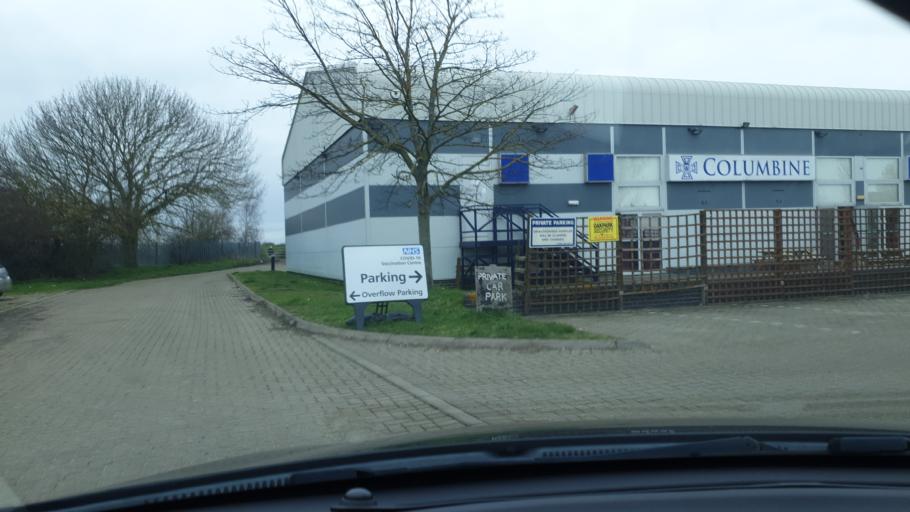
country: GB
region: England
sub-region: Essex
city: Walton-on-the-Naze
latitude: 51.8532
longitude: 1.2750
